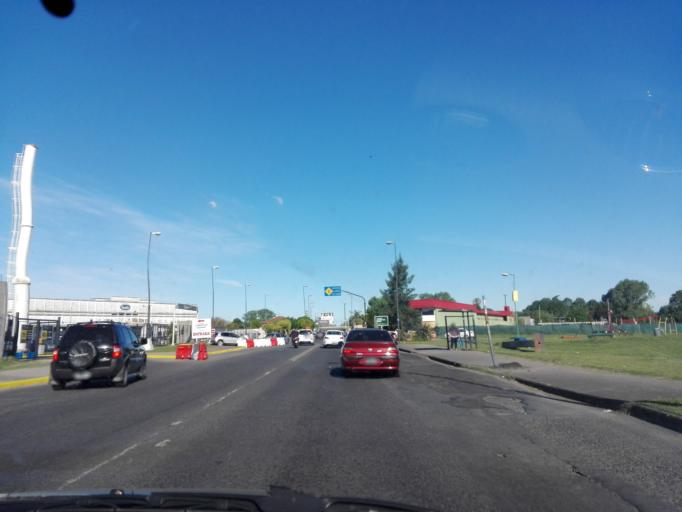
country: AR
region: Buenos Aires
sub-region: Partido de La Plata
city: La Plata
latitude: -34.8950
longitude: -57.9968
